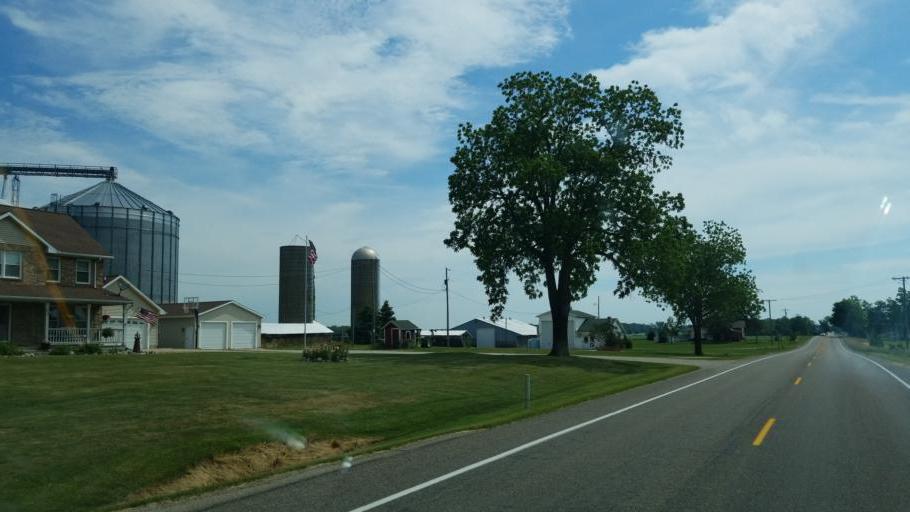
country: US
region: Michigan
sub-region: Eaton County
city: Charlotte
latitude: 42.6260
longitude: -84.8364
